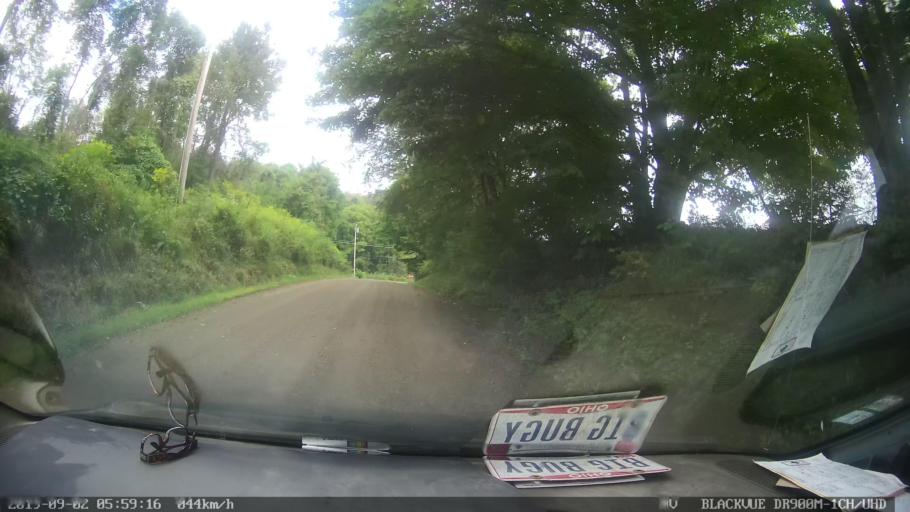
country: US
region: Ohio
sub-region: Knox County
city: Fredericktown
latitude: 40.5362
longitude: -82.6366
